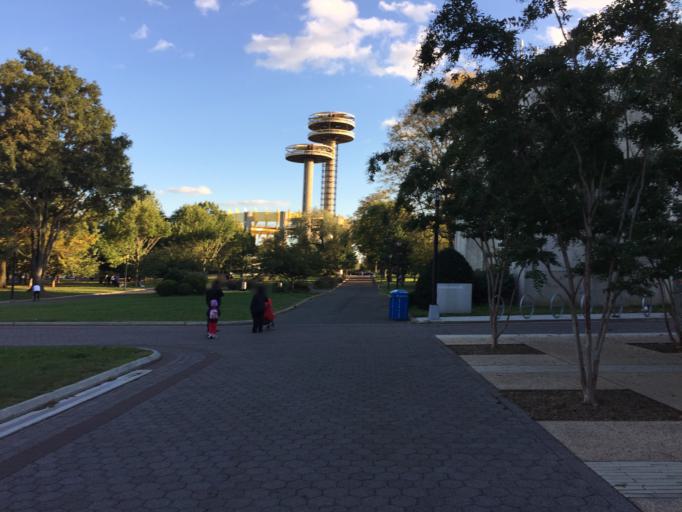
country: US
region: New York
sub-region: Queens County
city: Borough of Queens
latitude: 40.7459
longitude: -73.8463
